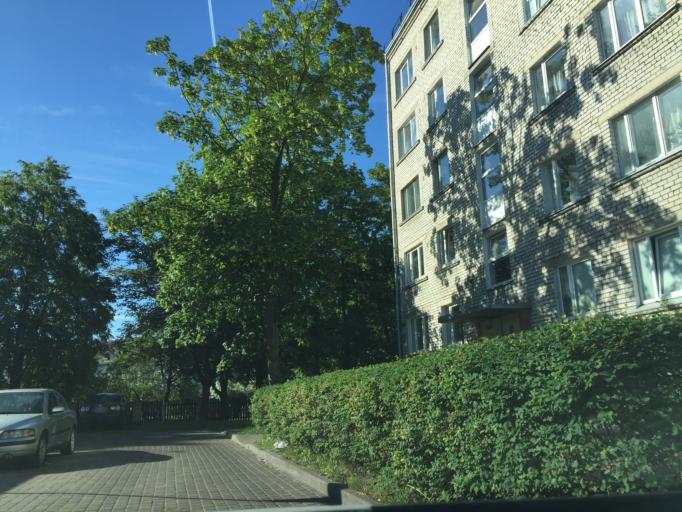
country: LV
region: Ventspils
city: Ventspils
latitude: 57.4011
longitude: 21.5875
